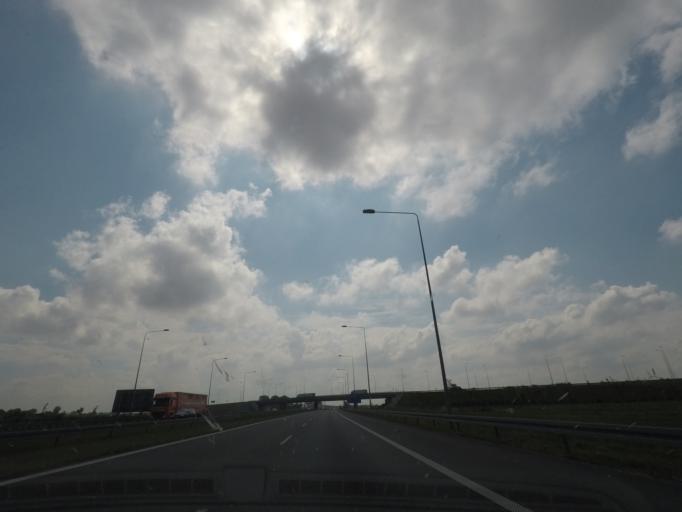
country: PL
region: Lodz Voivodeship
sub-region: Powiat kutnowski
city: Krzyzanow
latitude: 52.2207
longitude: 19.4705
